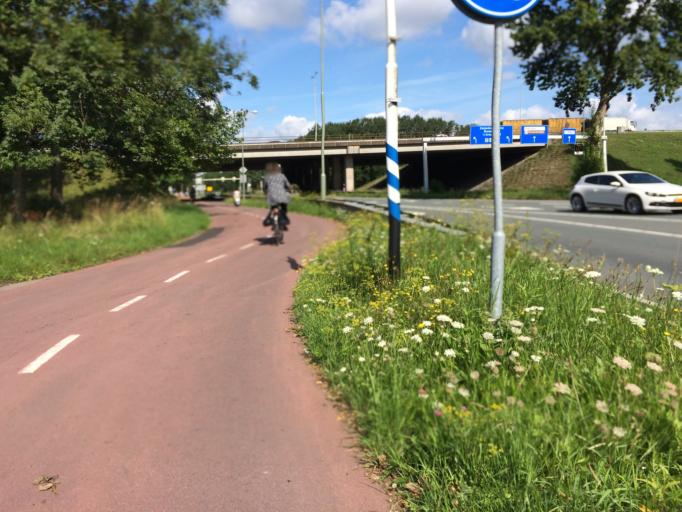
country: NL
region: South Holland
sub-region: Gemeente Dordrecht
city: Dordrecht
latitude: 51.8023
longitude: 4.6981
